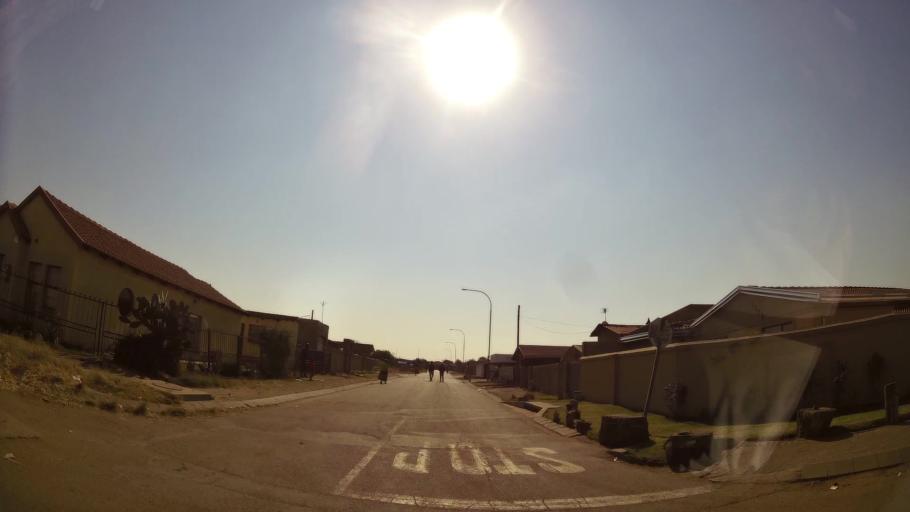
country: ZA
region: Gauteng
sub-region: Ekurhuleni Metropolitan Municipality
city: Benoni
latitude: -26.2293
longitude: 28.3020
